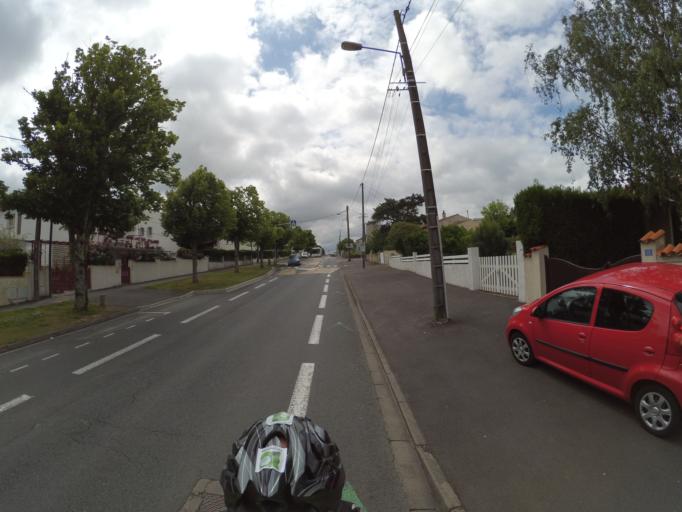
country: FR
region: Poitou-Charentes
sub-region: Departement de la Charente-Maritime
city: Rochefort
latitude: 45.9531
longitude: -0.9689
